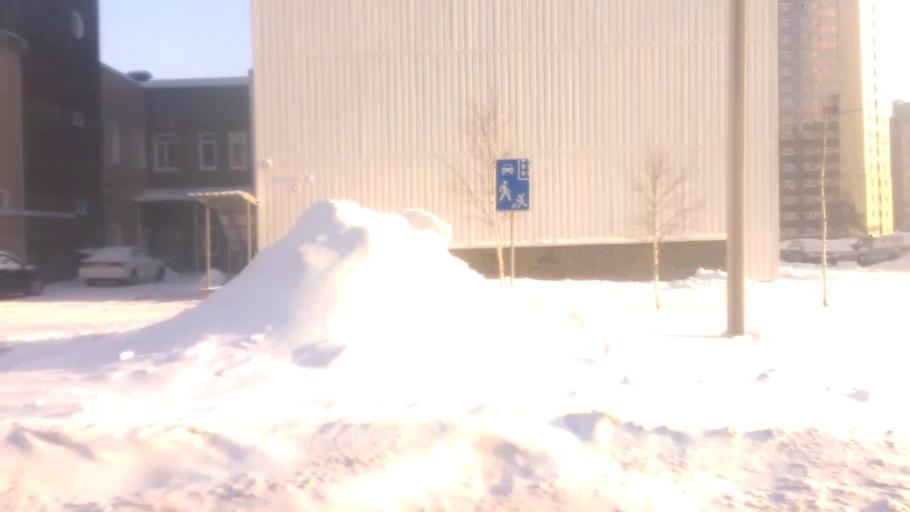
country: RU
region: Altai Krai
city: Novosilikatnyy
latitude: 53.3452
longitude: 83.6557
